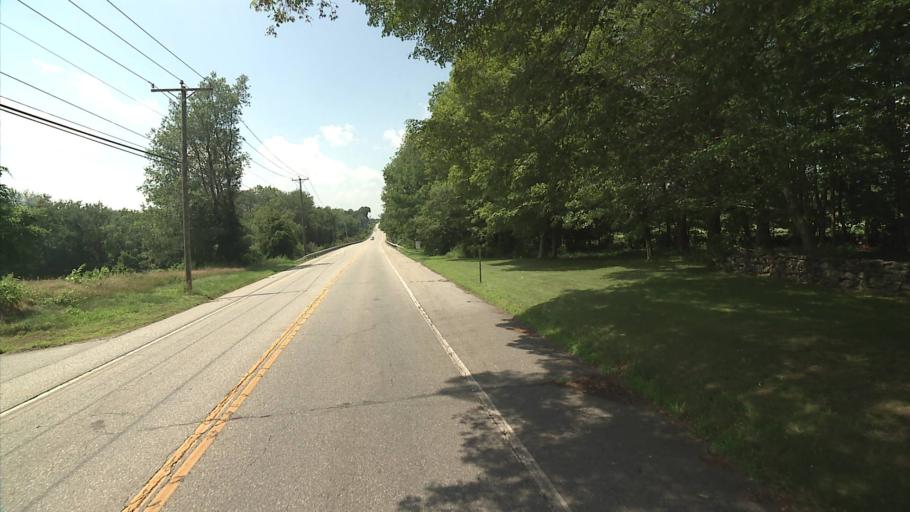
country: US
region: Connecticut
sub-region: New London County
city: Preston City
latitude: 41.5332
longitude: -72.0113
